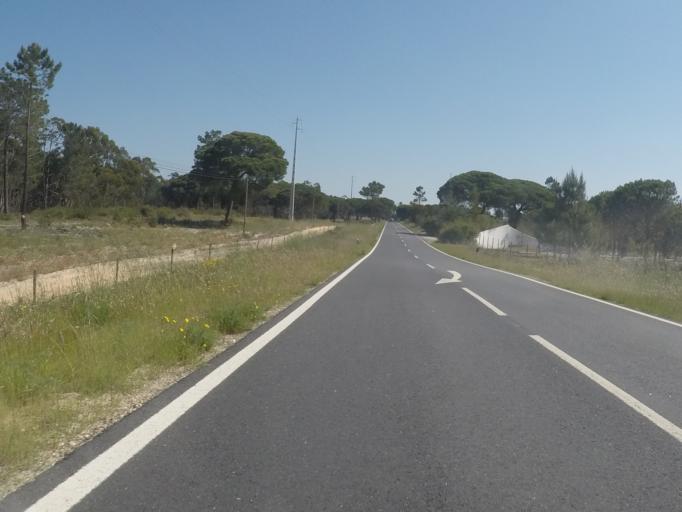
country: PT
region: Setubal
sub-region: Grandola
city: Grandola
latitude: 38.2581
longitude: -8.7352
